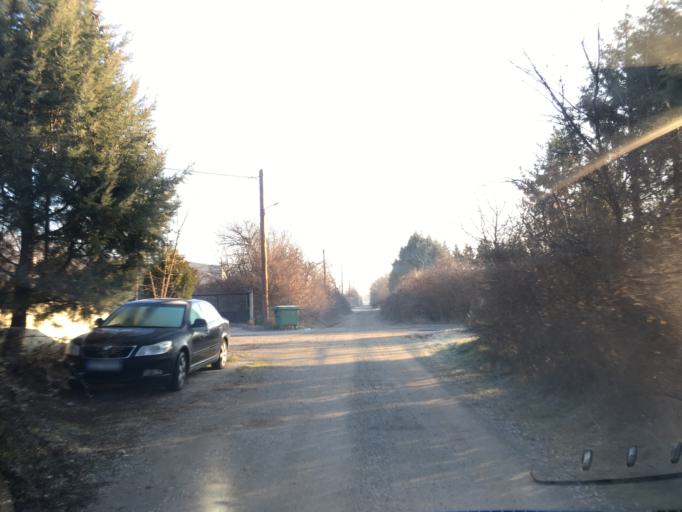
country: GR
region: West Macedonia
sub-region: Nomos Kozanis
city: Kozani
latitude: 40.2819
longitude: 21.7683
